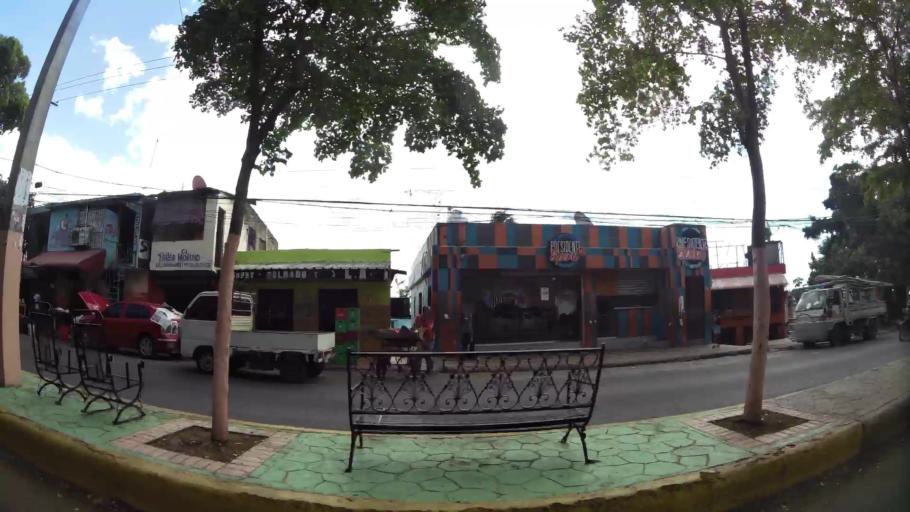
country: DO
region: Nacional
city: Ensanche Luperon
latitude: 18.4956
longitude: -69.8831
